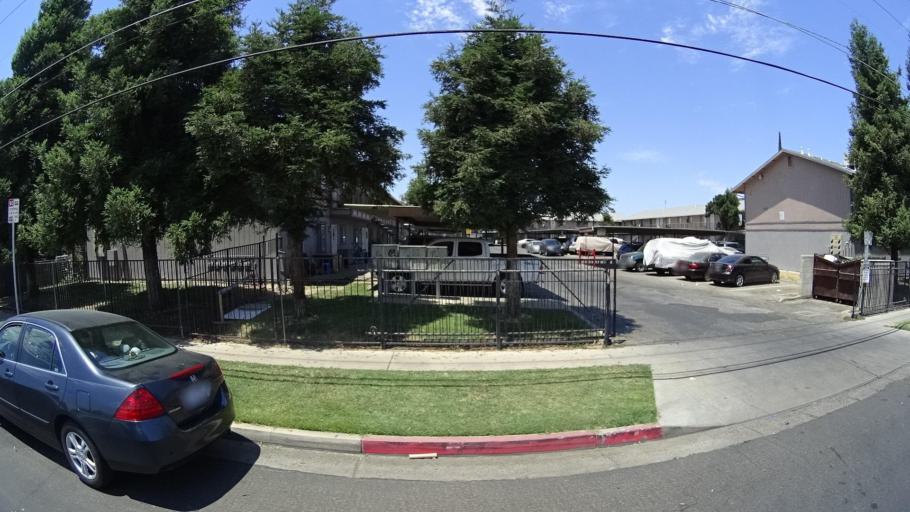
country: US
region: California
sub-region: Fresno County
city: Fresno
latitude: 36.7264
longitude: -119.7513
